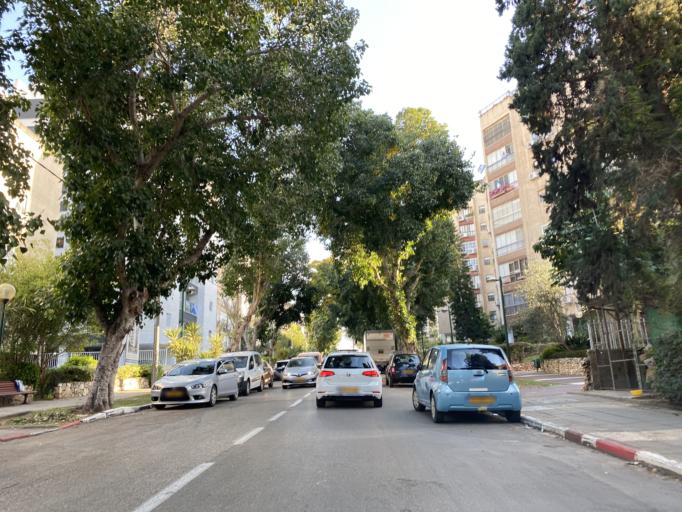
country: IL
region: Central District
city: Kfar Saba
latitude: 32.1724
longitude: 34.9135
